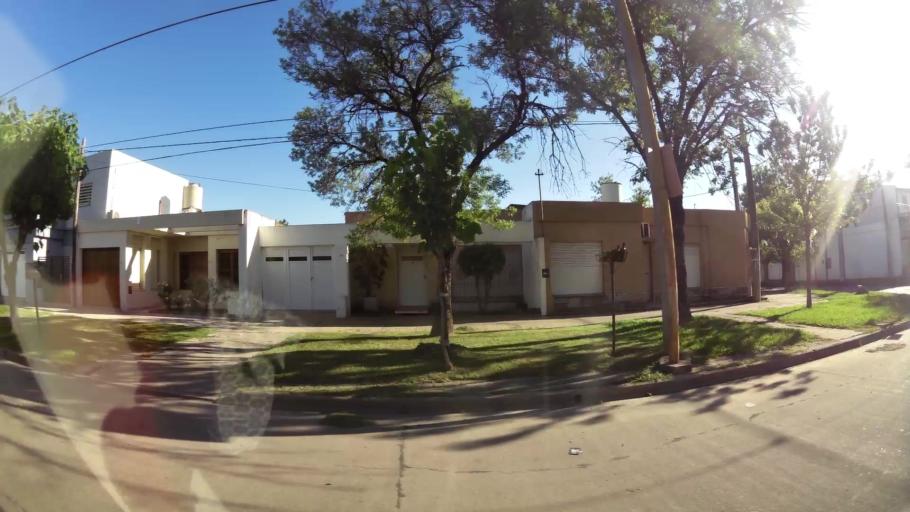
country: AR
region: Cordoba
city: San Francisco
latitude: -31.4333
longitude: -62.0709
